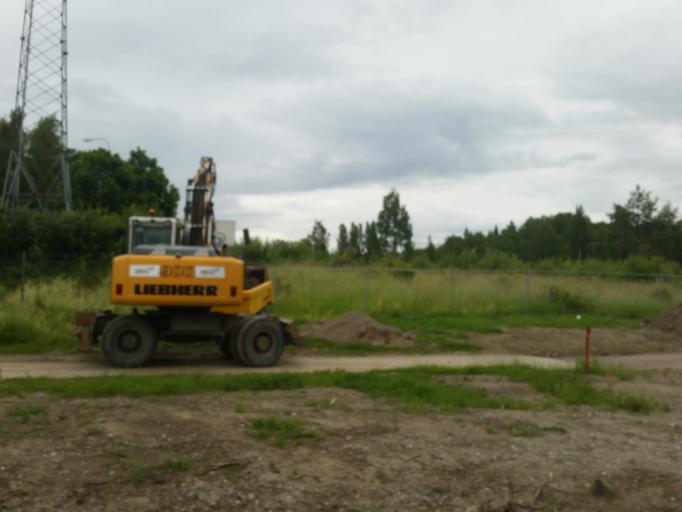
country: SE
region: Stockholm
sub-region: Stockholms Kommun
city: Kista
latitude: 59.4196
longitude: 17.9149
